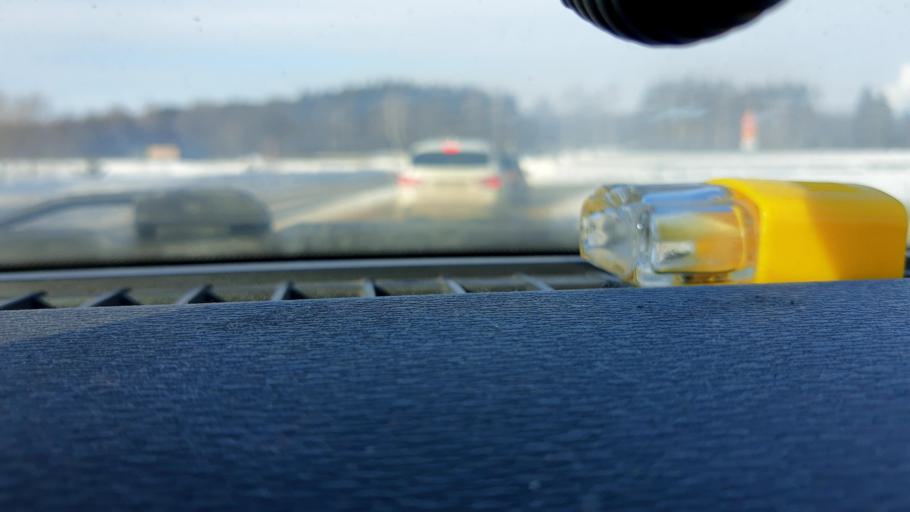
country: RU
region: Bashkortostan
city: Iglino
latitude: 54.7427
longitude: 56.3067
